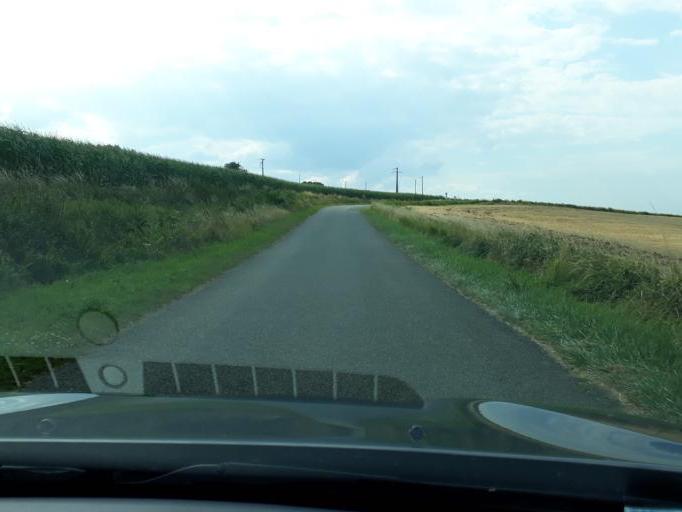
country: FR
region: Centre
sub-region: Departement du Cher
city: Jouet-sur-l'Aubois
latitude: 47.0244
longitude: 2.9033
